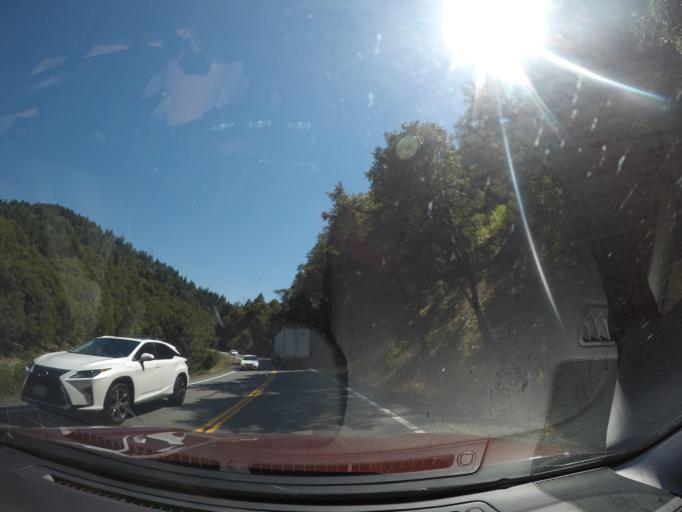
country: US
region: California
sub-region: Shasta County
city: Bella Vista
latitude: 40.7314
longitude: -122.0765
